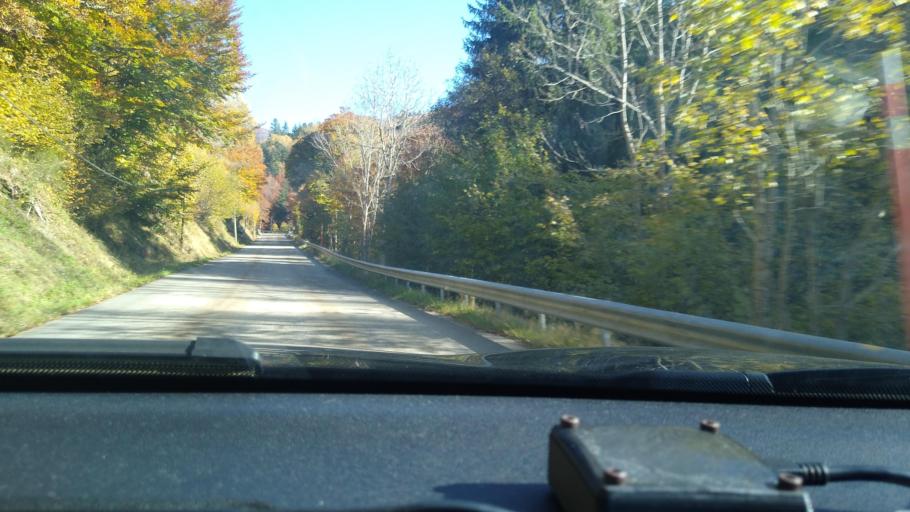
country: FR
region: Midi-Pyrenees
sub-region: Departement de l'Ariege
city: Ax-les-Thermes
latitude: 42.7164
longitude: 1.9212
